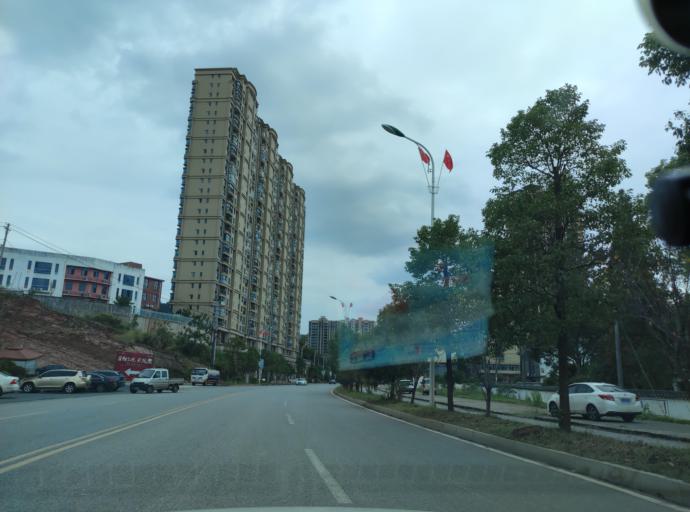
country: CN
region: Jiangxi Sheng
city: Pingxiang
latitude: 27.6803
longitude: 113.9091
